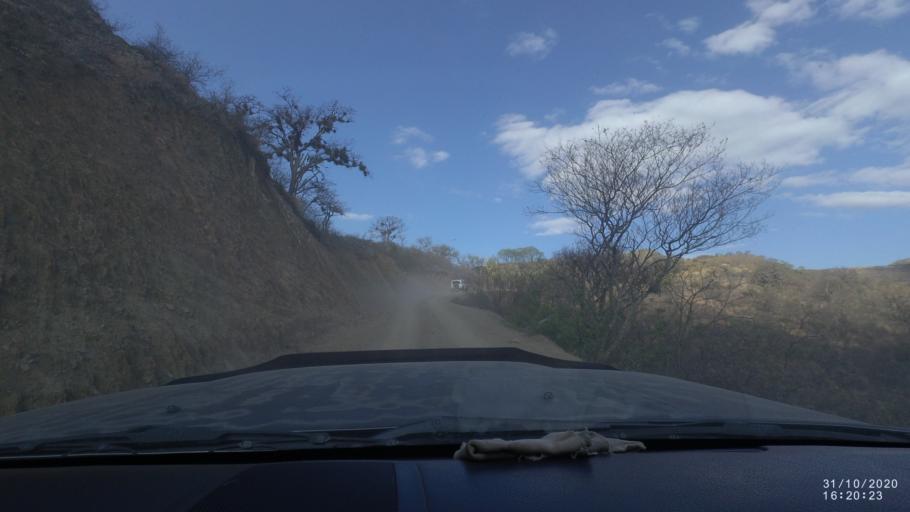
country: BO
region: Chuquisaca
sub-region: Provincia Zudanez
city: Mojocoya
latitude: -18.3978
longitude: -64.6019
